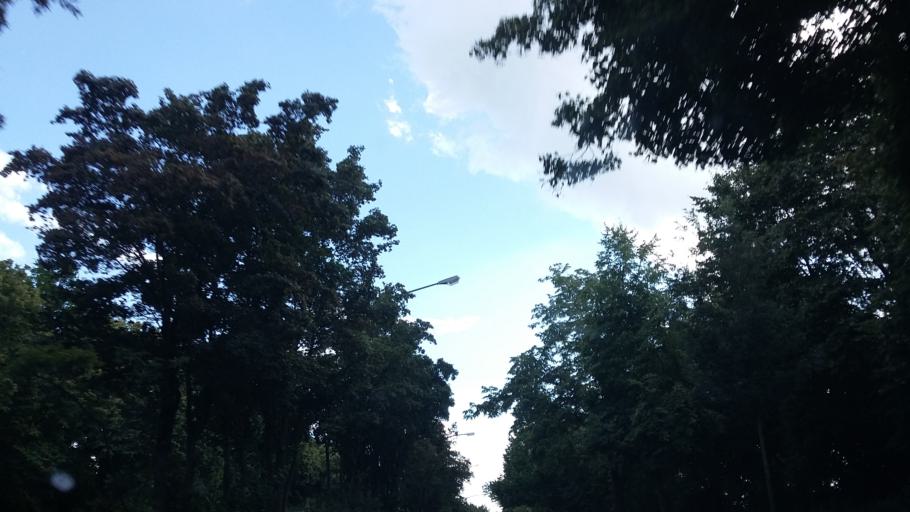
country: DE
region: Bavaria
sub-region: Swabia
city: Augsburg
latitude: 48.3910
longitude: 10.9119
